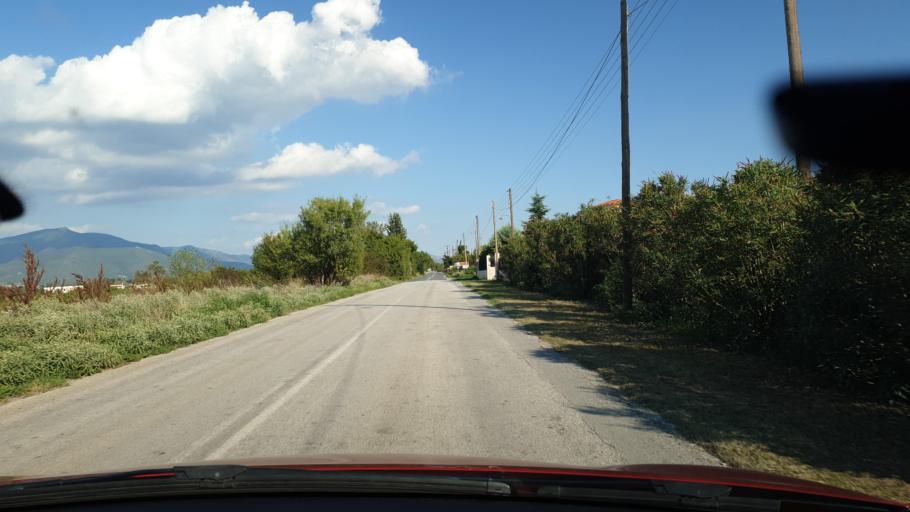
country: GR
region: Central Macedonia
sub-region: Nomos Thessalonikis
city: Agia Paraskevi
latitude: 40.4801
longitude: 23.0695
